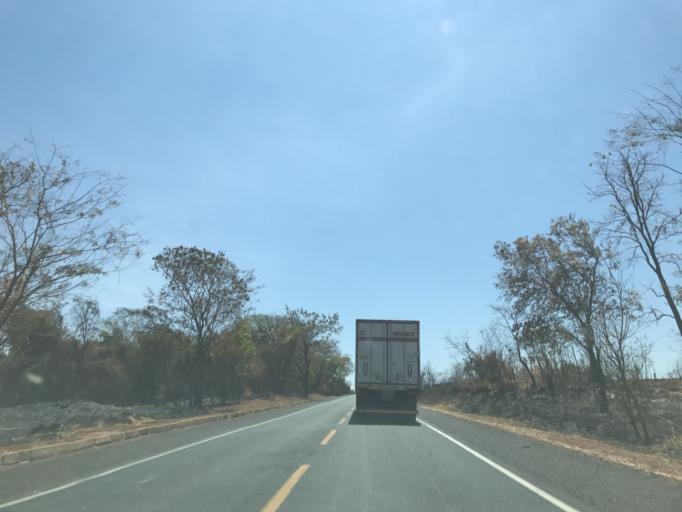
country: BR
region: Minas Gerais
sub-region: Prata
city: Prata
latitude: -19.5040
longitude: -48.8484
